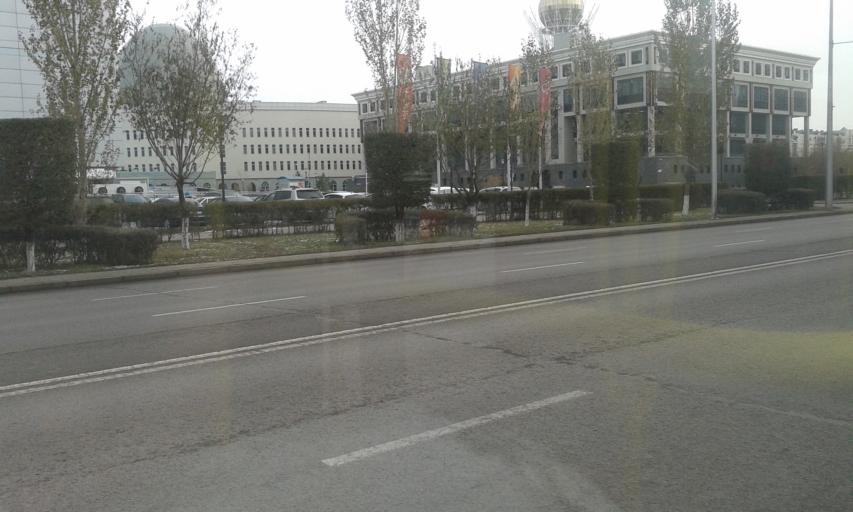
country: KZ
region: Astana Qalasy
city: Astana
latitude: 51.1271
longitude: 71.4254
